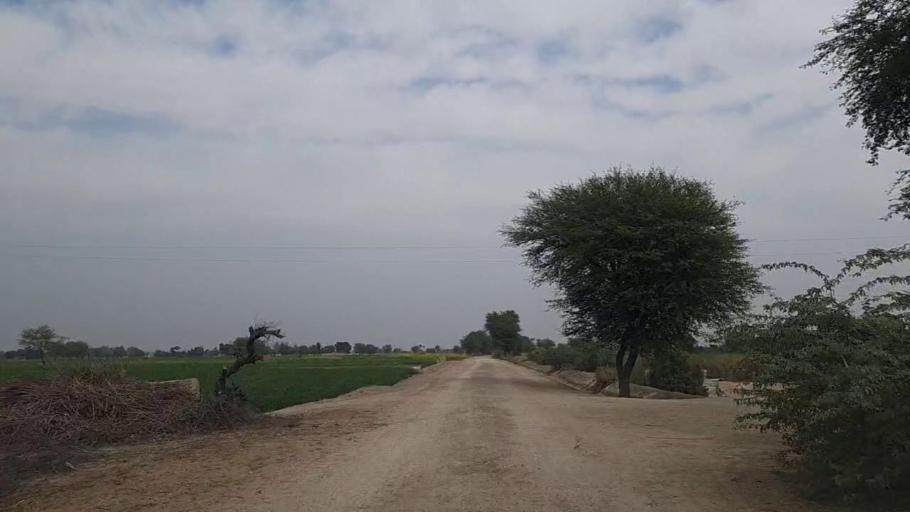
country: PK
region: Sindh
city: Daur
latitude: 26.4286
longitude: 68.4628
